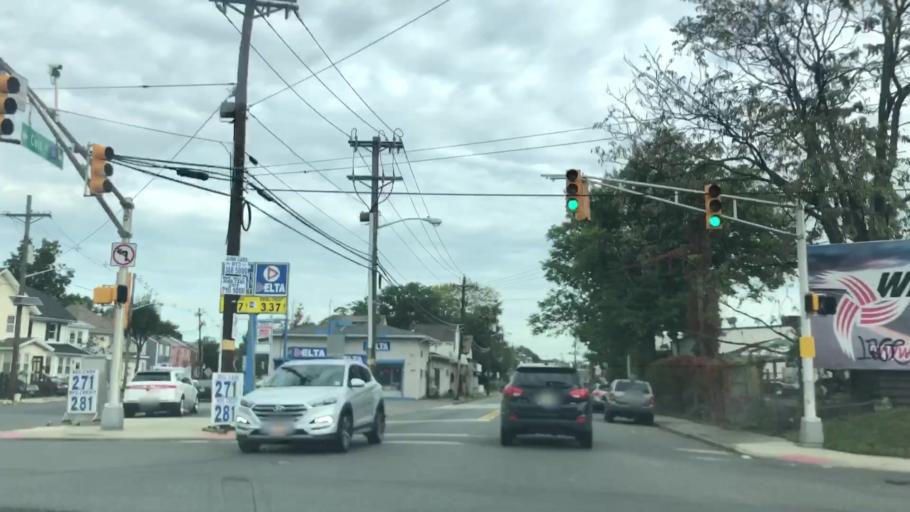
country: US
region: New Jersey
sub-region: Union County
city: Hillside
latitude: 40.7097
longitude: -74.2323
